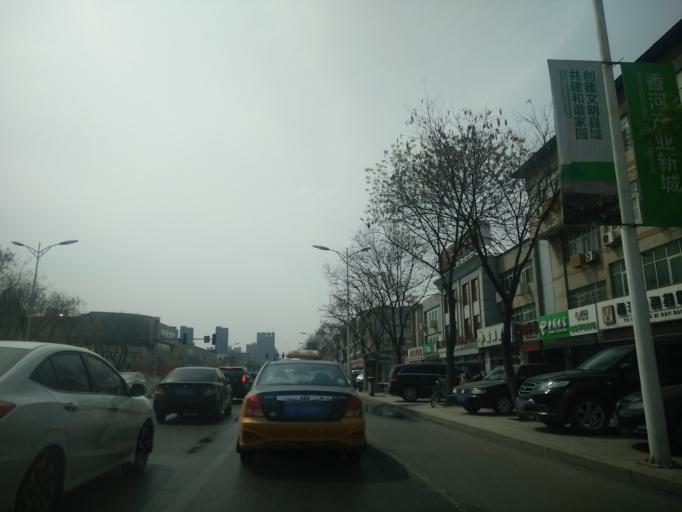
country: CN
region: Beijing
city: Xiji
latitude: 39.7633
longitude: 117.0001
